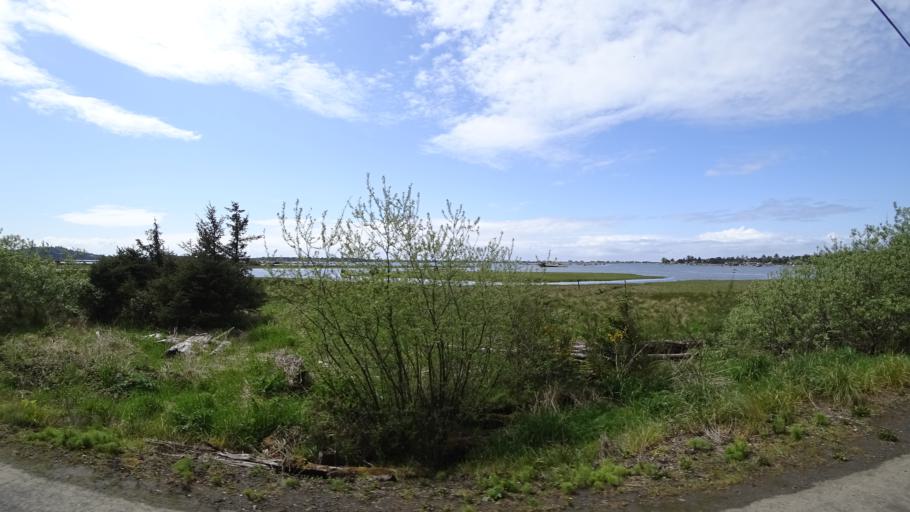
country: US
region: Oregon
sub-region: Lincoln County
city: Lincoln City
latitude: 44.9070
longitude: -124.0062
